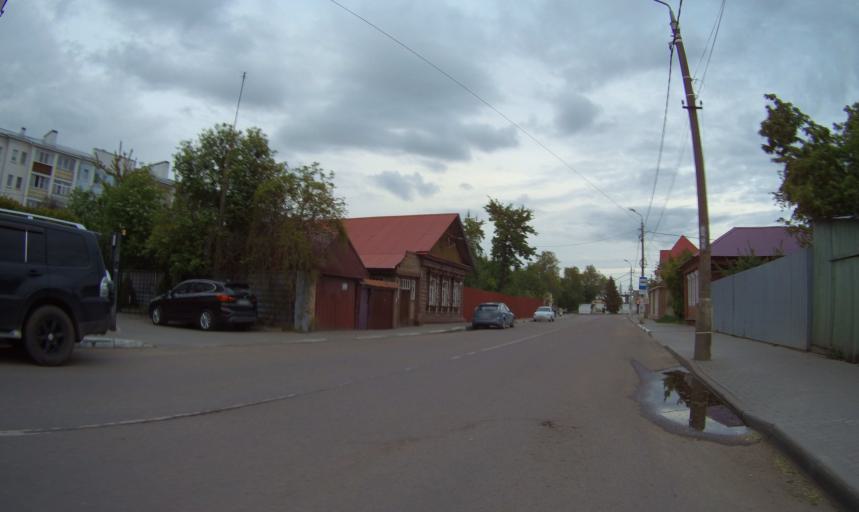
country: RU
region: Moskovskaya
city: Kolomna
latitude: 55.0992
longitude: 38.7741
